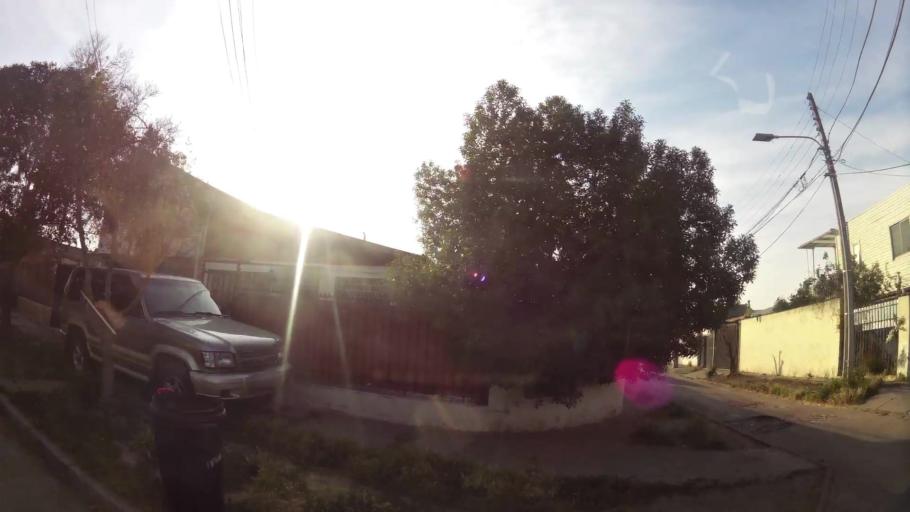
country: CL
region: Santiago Metropolitan
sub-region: Provincia de Santiago
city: La Pintana
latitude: -33.5279
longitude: -70.6671
